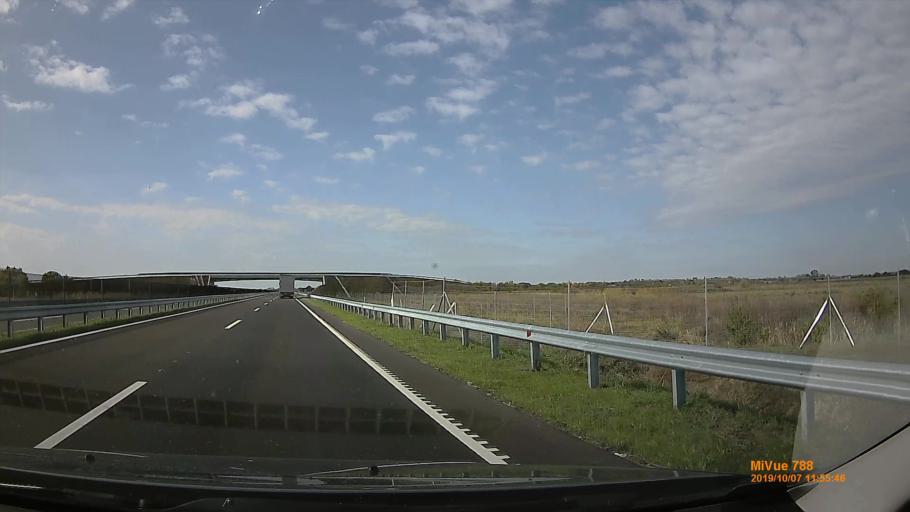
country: HU
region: Bekes
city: Szarvas
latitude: 46.8187
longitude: 20.5652
